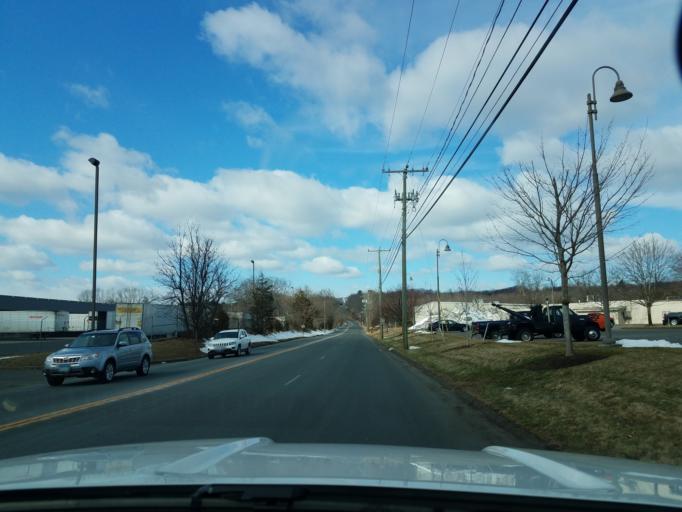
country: US
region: Connecticut
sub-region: Hartford County
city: Plainville
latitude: 41.6410
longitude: -72.8763
